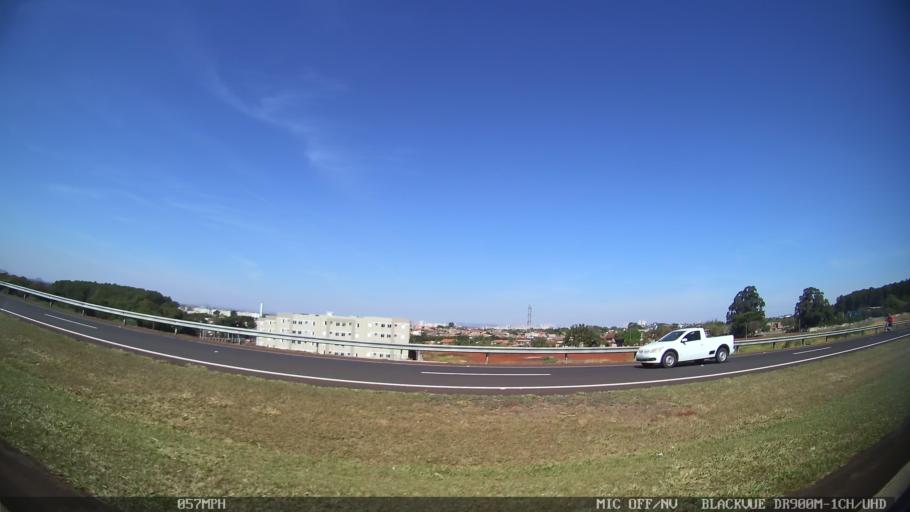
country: BR
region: Sao Paulo
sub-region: Ribeirao Preto
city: Ribeirao Preto
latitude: -21.1177
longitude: -47.8289
